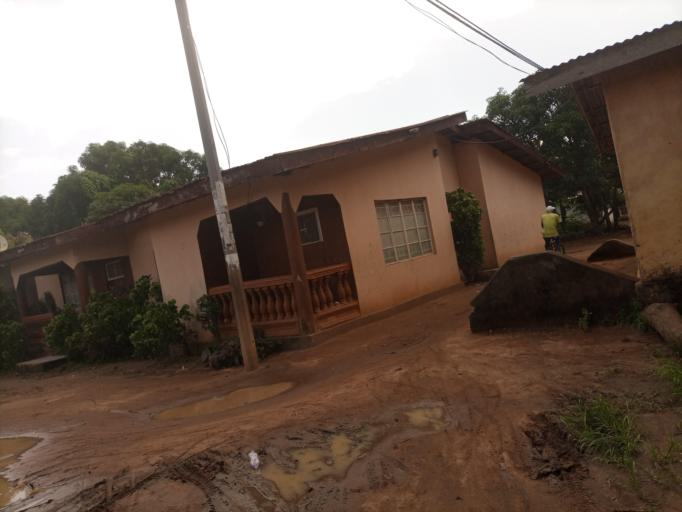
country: SL
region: Northern Province
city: Tintafor
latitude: 8.6354
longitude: -13.2144
